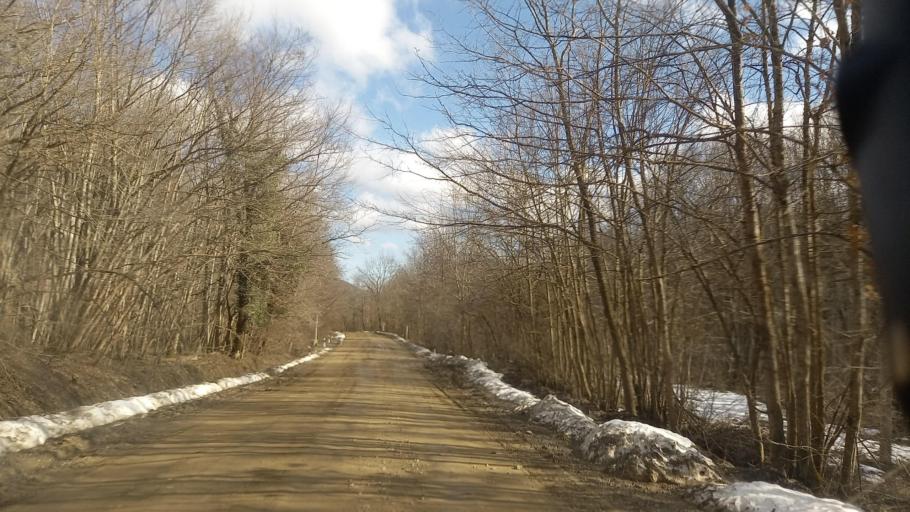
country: RU
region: Krasnodarskiy
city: Smolenskaya
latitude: 44.6057
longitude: 38.7781
